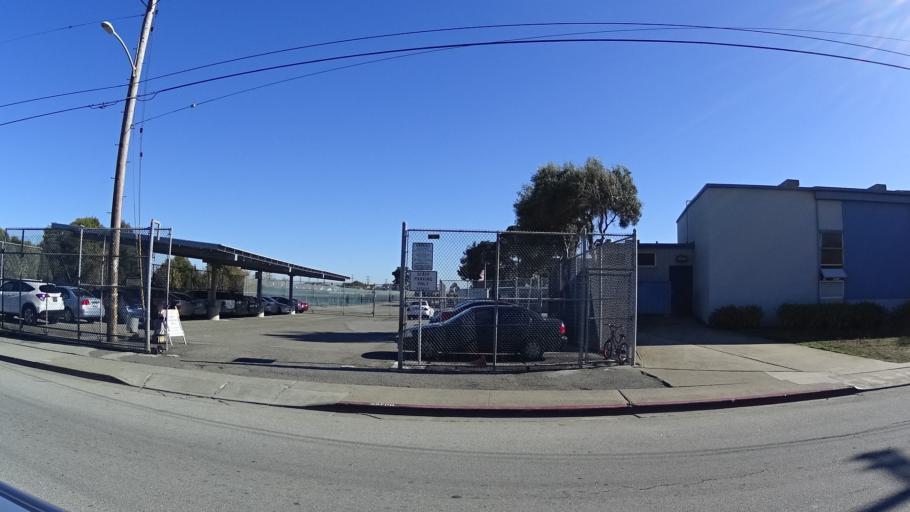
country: US
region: California
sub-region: San Mateo County
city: South San Francisco
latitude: 37.6516
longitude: -122.4274
